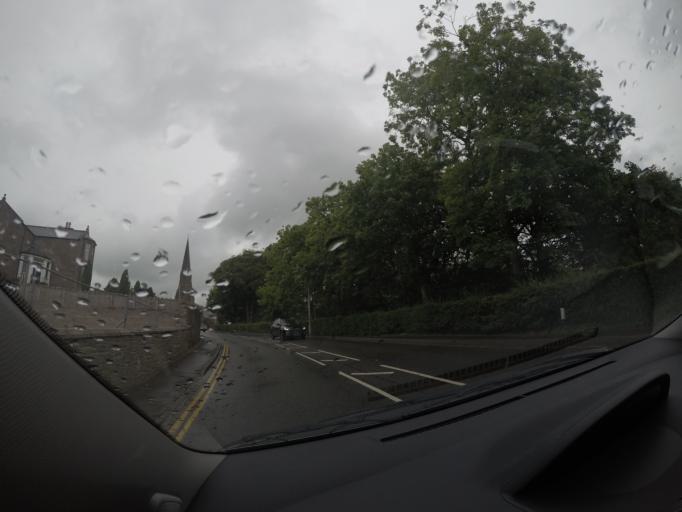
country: GB
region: Scotland
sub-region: Angus
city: Brechin
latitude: 56.7330
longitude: -2.6549
